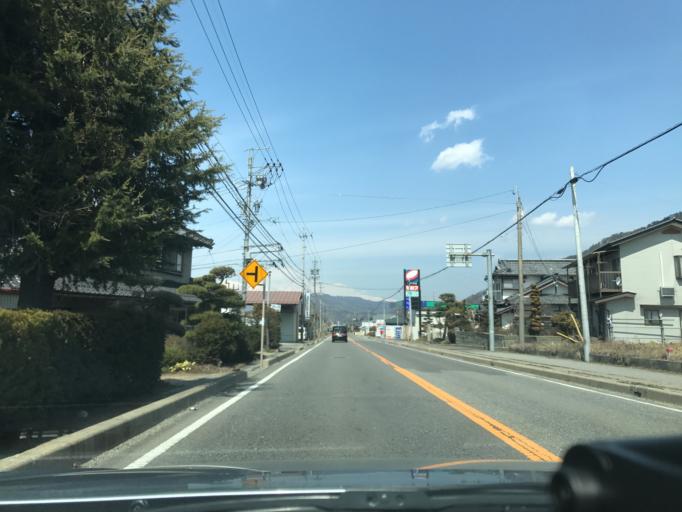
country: JP
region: Nagano
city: Toyoshina
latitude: 36.3248
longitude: 137.9301
